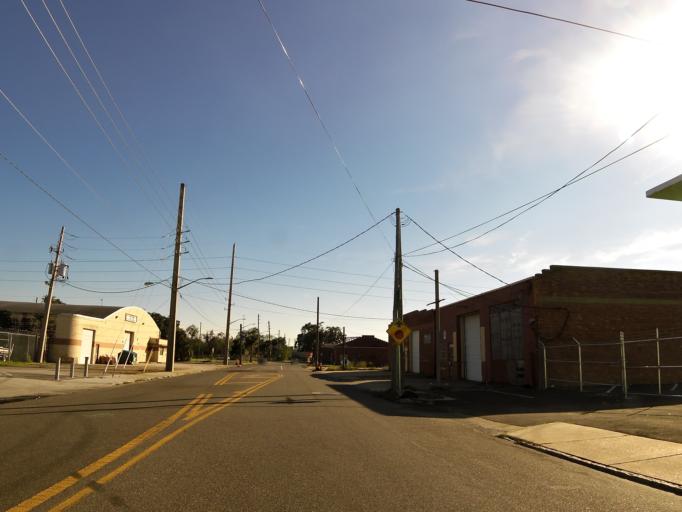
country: US
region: Florida
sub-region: Duval County
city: Jacksonville
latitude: 30.3346
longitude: -81.6760
